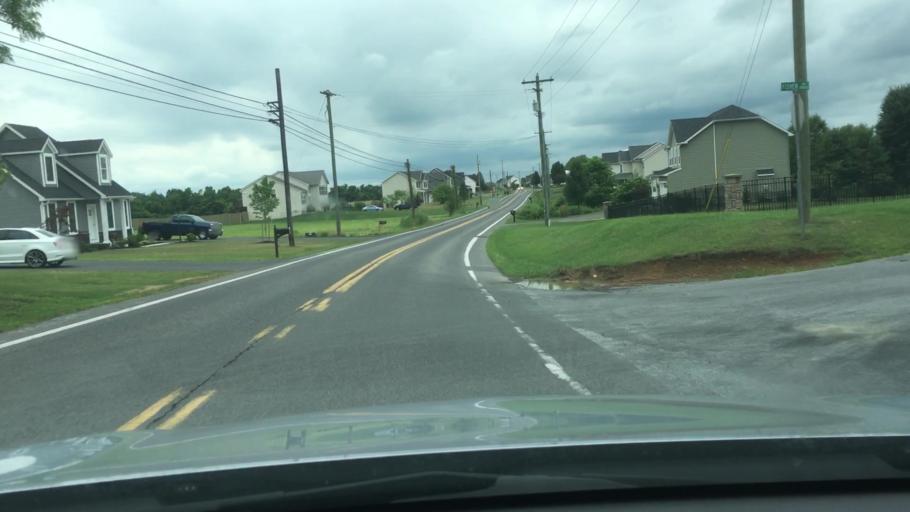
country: US
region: Pennsylvania
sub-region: Franklin County
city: Chambersburg
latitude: 39.9012
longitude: -77.7190
